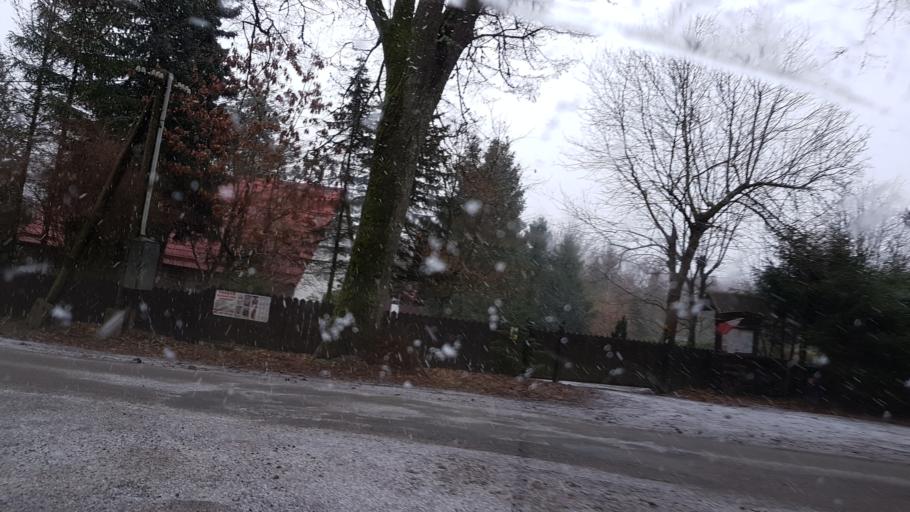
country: PL
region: West Pomeranian Voivodeship
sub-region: Powiat slawienski
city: Slawno
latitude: 54.2557
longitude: 16.5788
